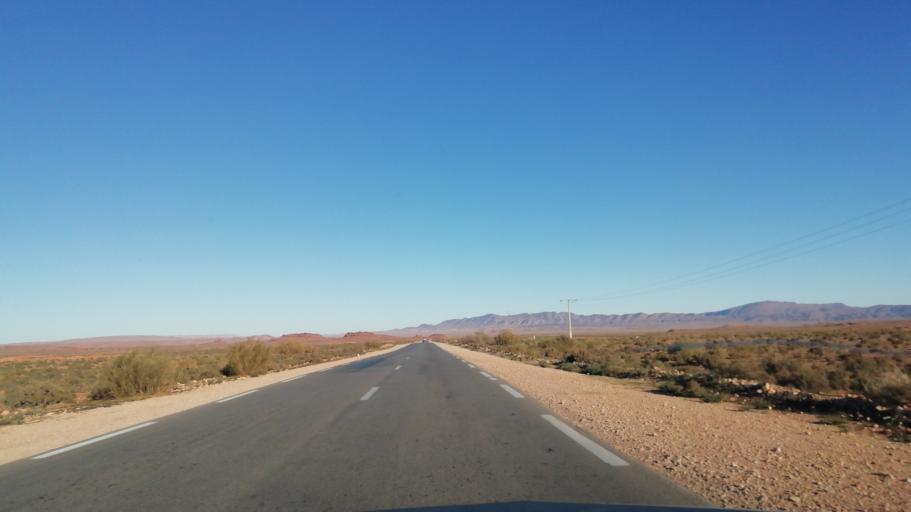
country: DZ
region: El Bayadh
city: El Abiodh Sidi Cheikh
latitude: 33.1686
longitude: 0.4778
